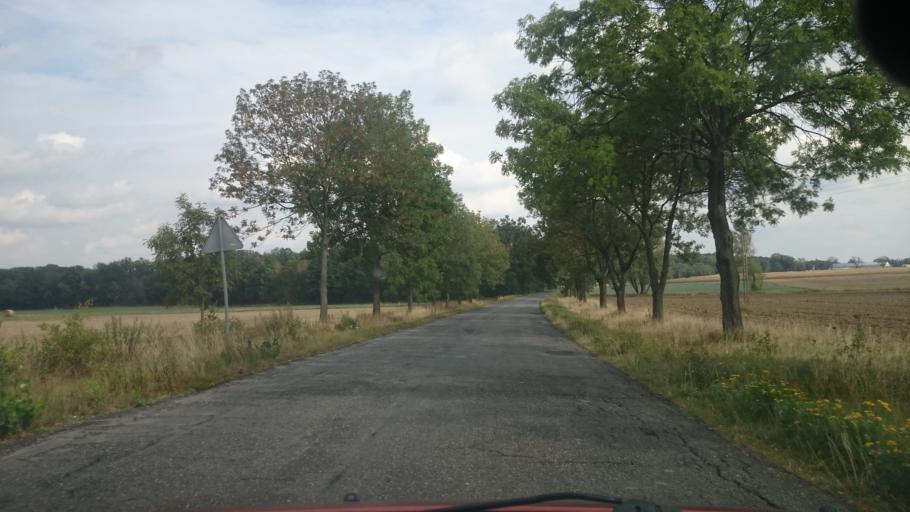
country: PL
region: Opole Voivodeship
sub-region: Powiat nyski
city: Otmuchow
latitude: 50.4988
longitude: 17.2289
